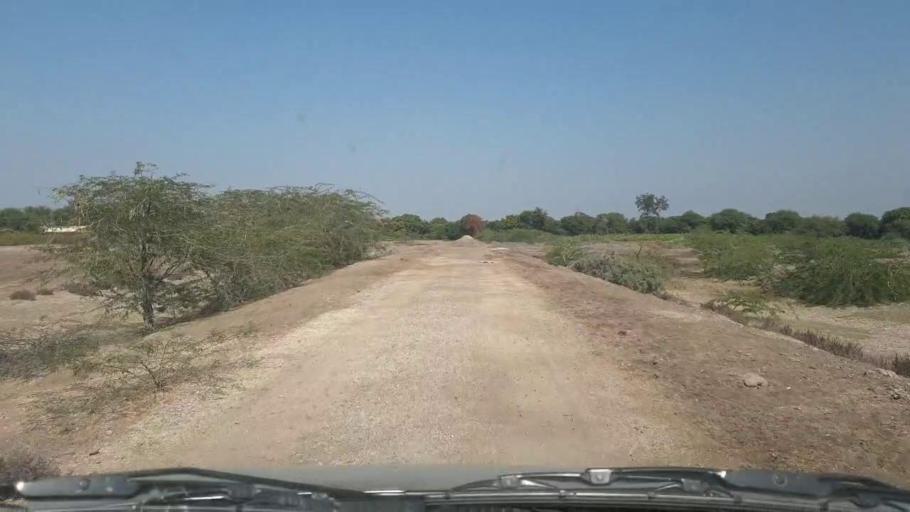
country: PK
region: Sindh
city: Samaro
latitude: 25.2434
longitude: 69.3262
